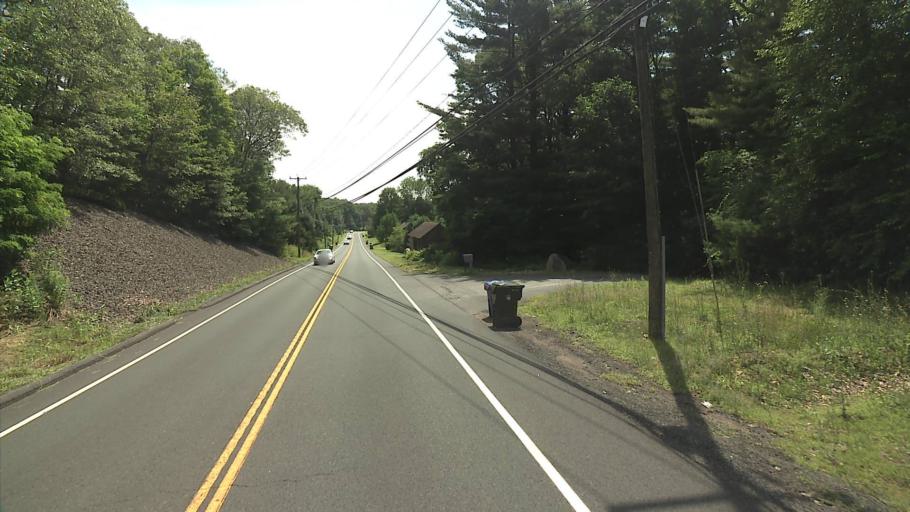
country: US
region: Connecticut
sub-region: Tolland County
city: Rockville
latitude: 41.8397
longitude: -72.4134
